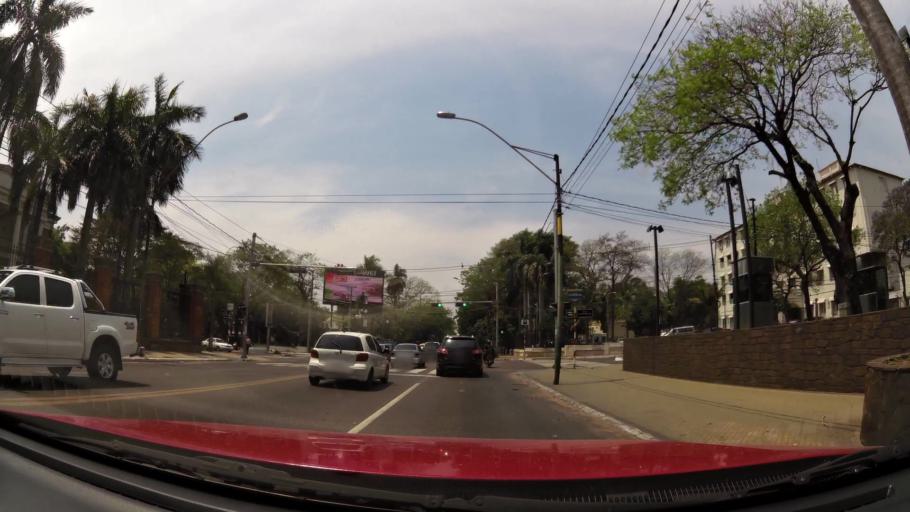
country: PY
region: Asuncion
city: Asuncion
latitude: -25.2926
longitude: -57.6036
